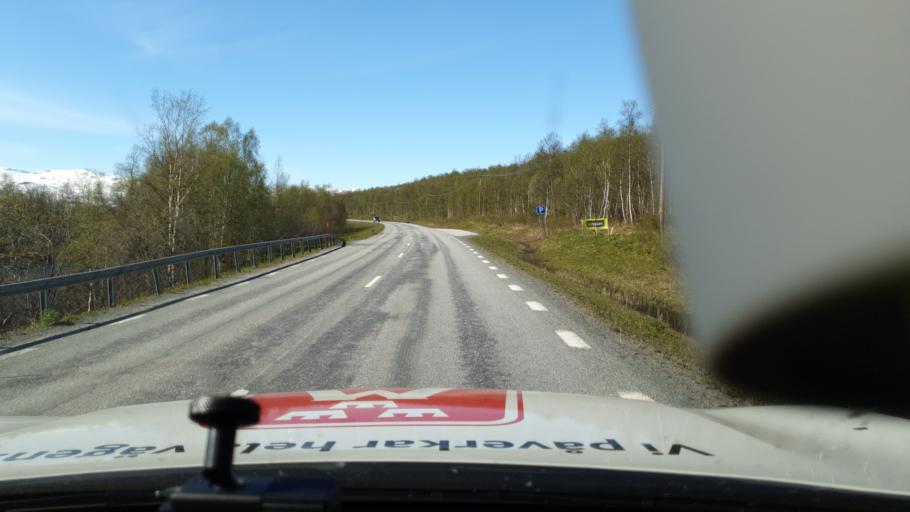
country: NO
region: Nordland
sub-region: Rana
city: Mo i Rana
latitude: 65.7998
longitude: 15.0969
